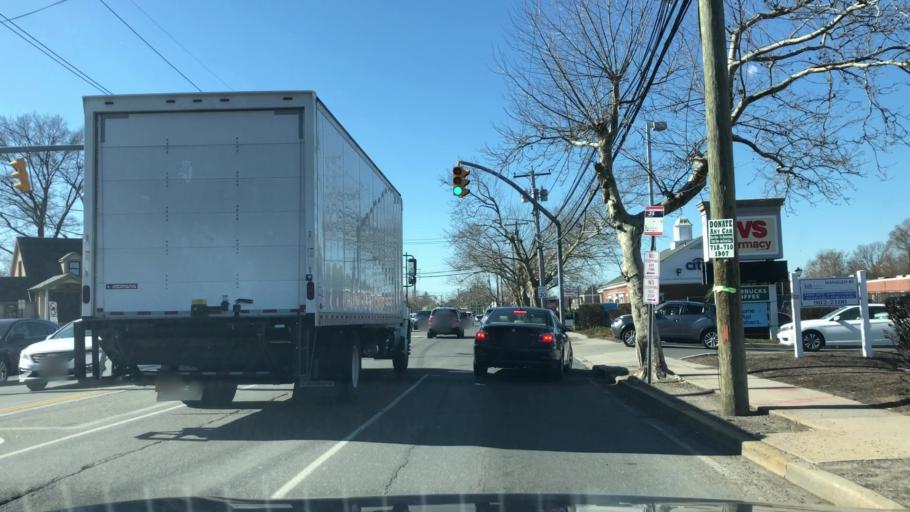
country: US
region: New York
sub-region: Nassau County
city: Malverne
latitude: 40.6908
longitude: -73.6850
